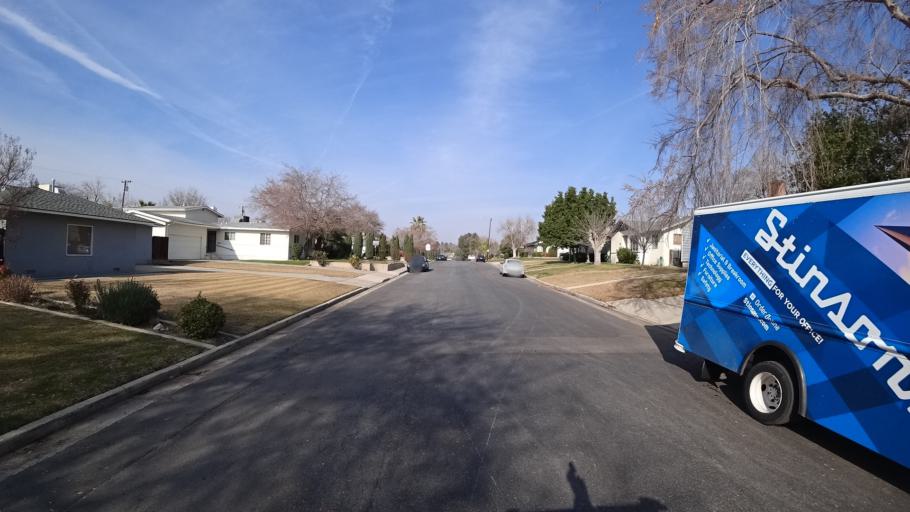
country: US
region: California
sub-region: Kern County
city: Oildale
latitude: 35.4002
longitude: -118.9808
